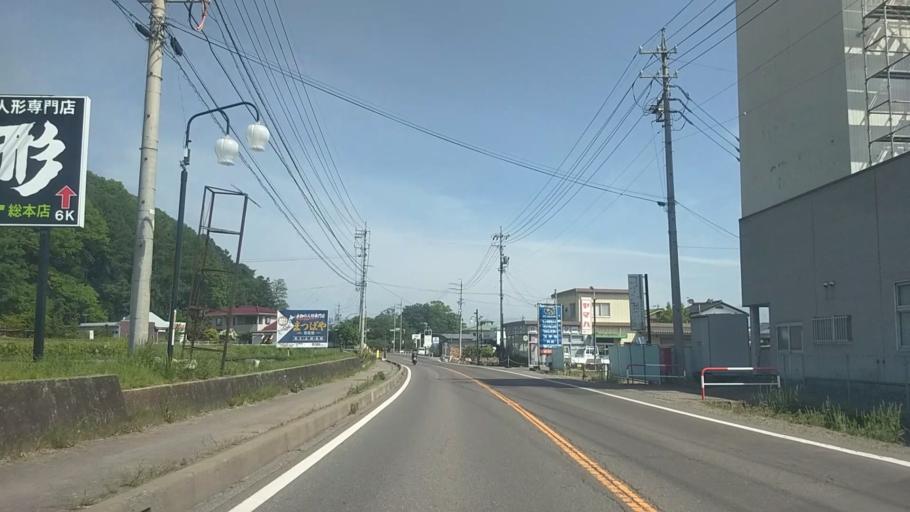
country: JP
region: Nagano
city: Saku
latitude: 36.1762
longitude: 138.4849
